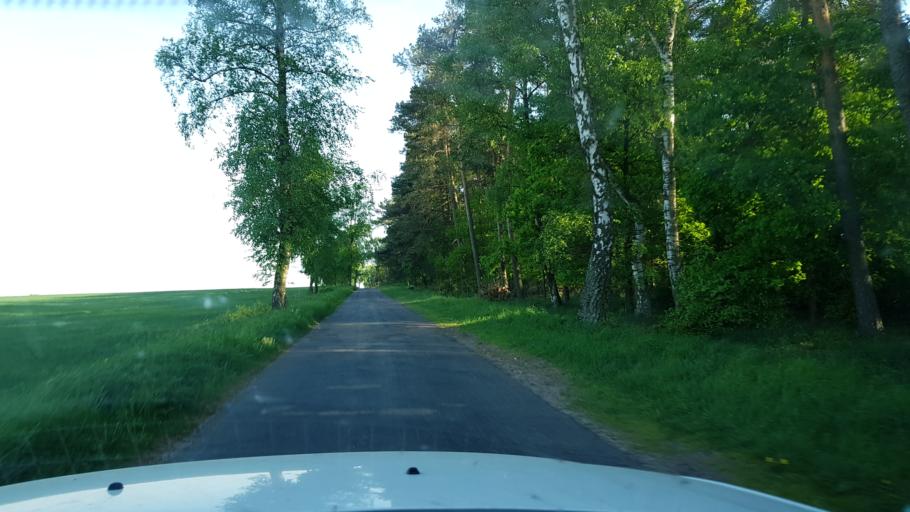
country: PL
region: West Pomeranian Voivodeship
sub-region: Powiat lobeski
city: Dobra
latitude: 53.6069
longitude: 15.3302
